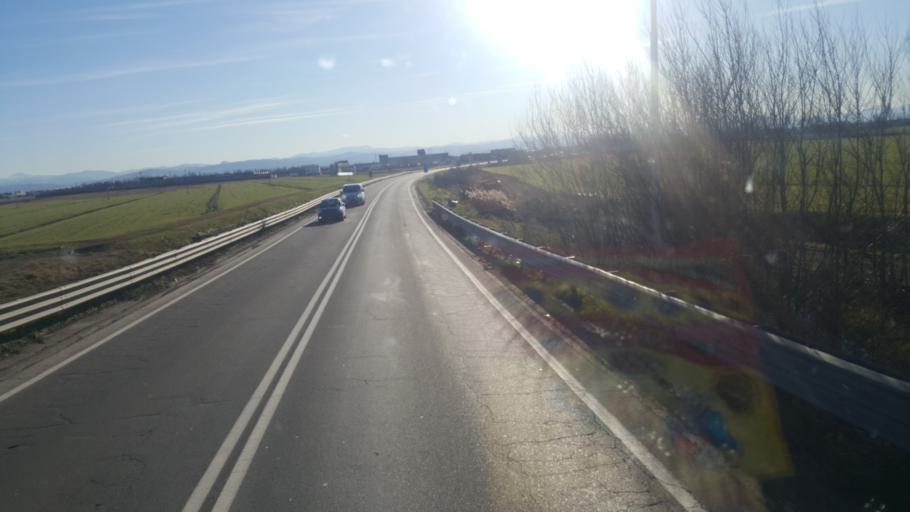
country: IT
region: Emilia-Romagna
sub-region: Provincia di Reggio Emilia
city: Bagnolo in Piano
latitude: 44.7554
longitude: 10.6573
